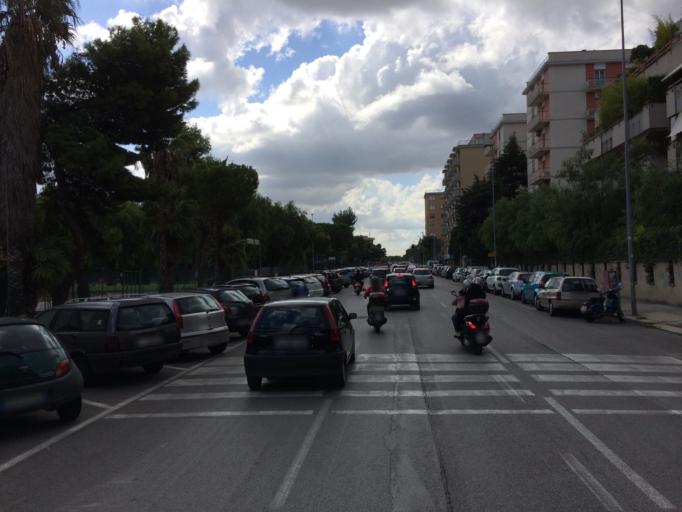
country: IT
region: Apulia
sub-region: Provincia di Bari
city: Bari
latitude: 41.1048
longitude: 16.8736
